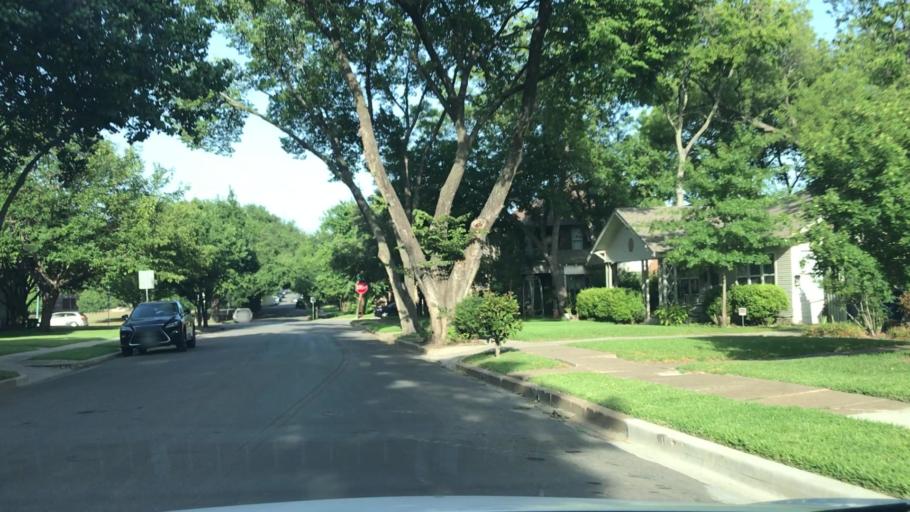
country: US
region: Texas
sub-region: Dallas County
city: Highland Park
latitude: 32.8220
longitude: -96.7624
